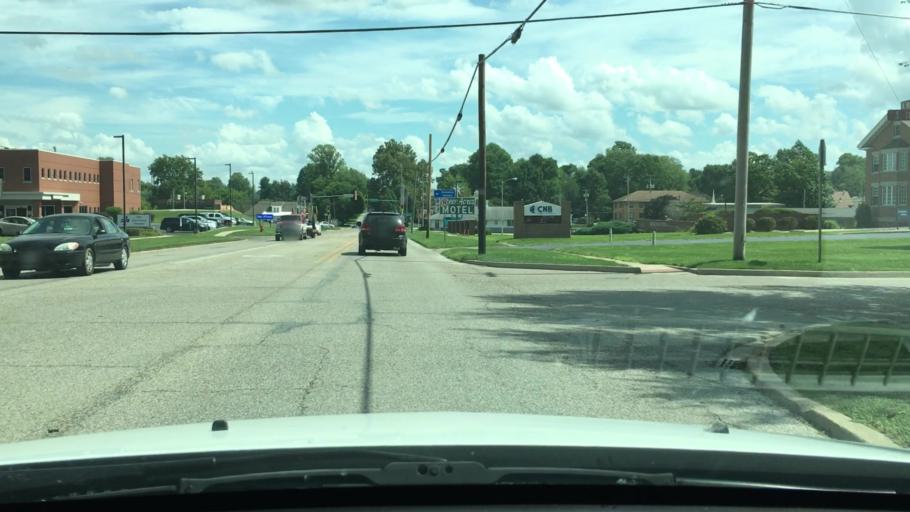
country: US
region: Illinois
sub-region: Pike County
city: Pittsfield
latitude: 39.6068
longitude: -90.8161
